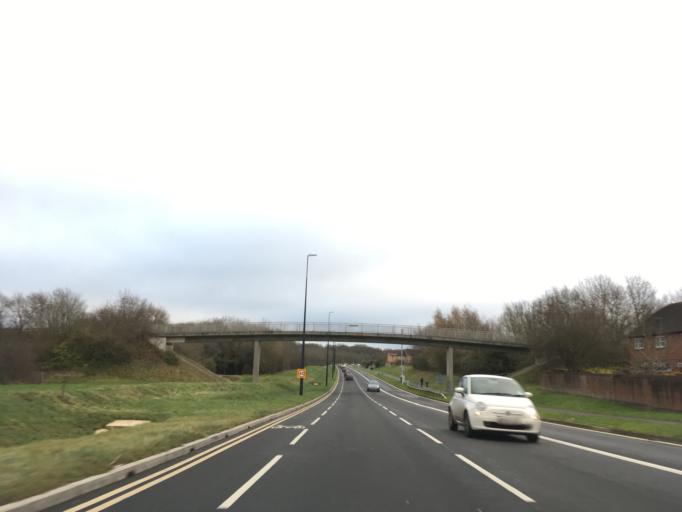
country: GB
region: England
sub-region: South Gloucestershire
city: Almondsbury
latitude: 51.5412
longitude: -2.5562
